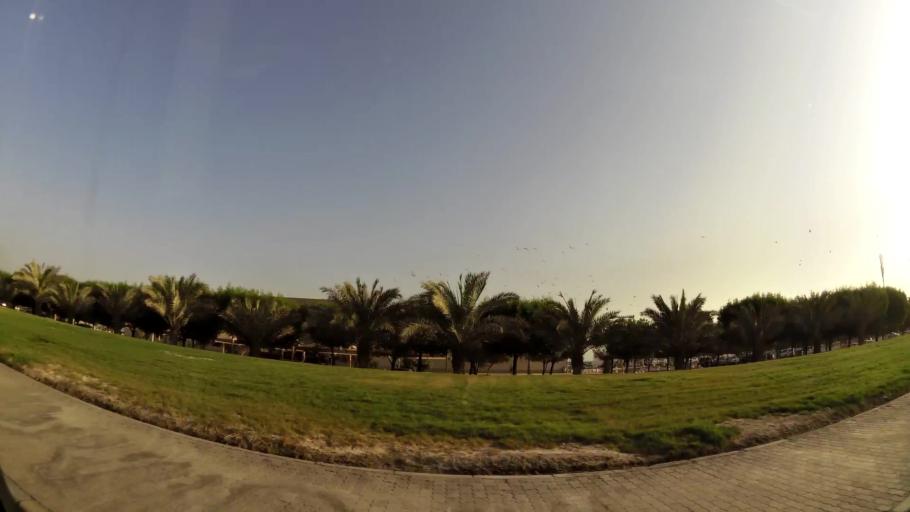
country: KW
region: Muhafazat Hawalli
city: Hawalli
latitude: 29.3403
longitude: 48.0519
